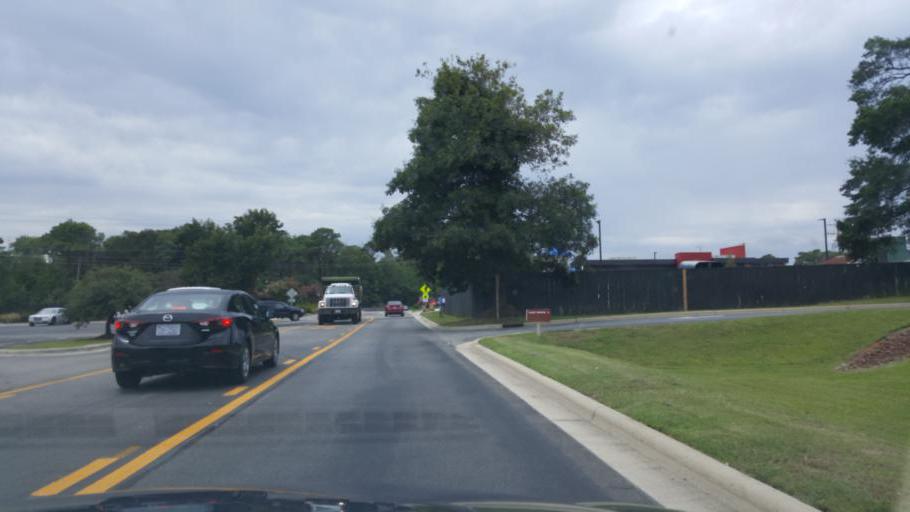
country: US
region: North Carolina
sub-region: Dare County
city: Kitty Hawk
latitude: 36.0979
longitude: -75.7216
